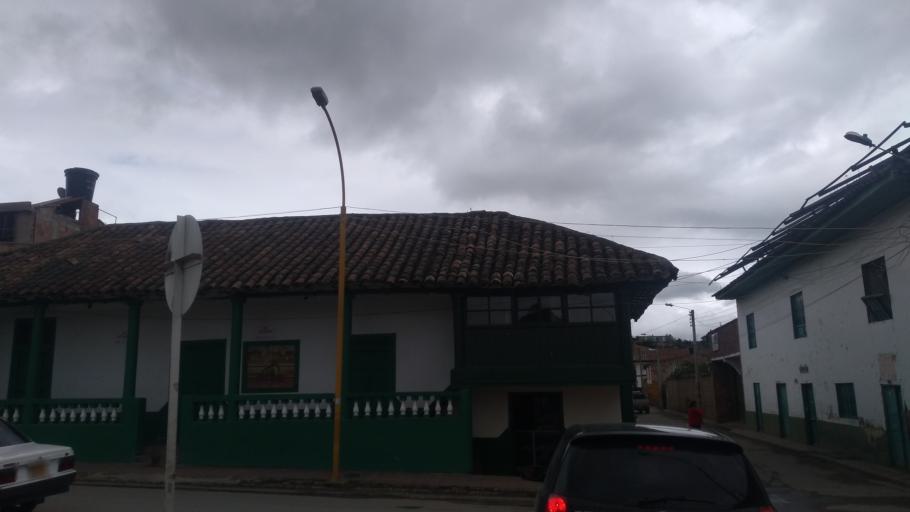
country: CO
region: Boyaca
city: Toca
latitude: 5.5644
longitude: -73.1851
